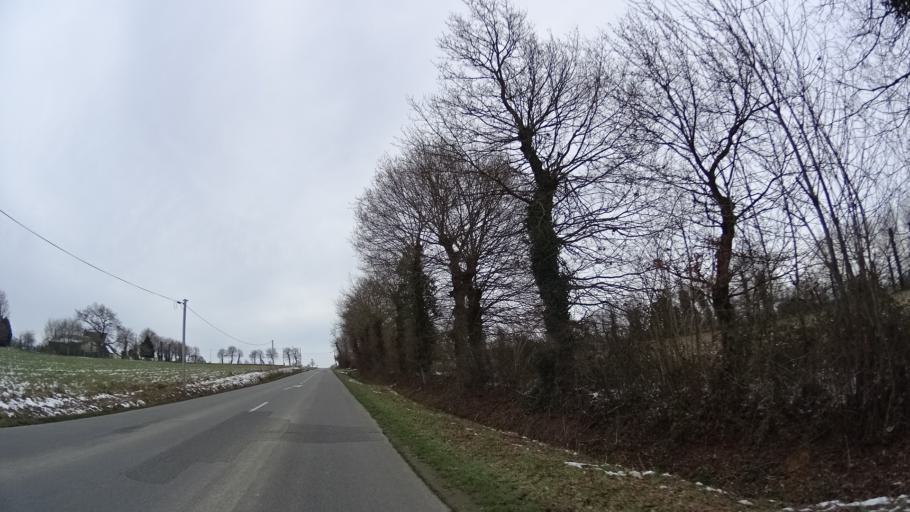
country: FR
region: Brittany
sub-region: Departement d'Ille-et-Vilaine
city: Irodouer
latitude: 48.2681
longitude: -1.9795
